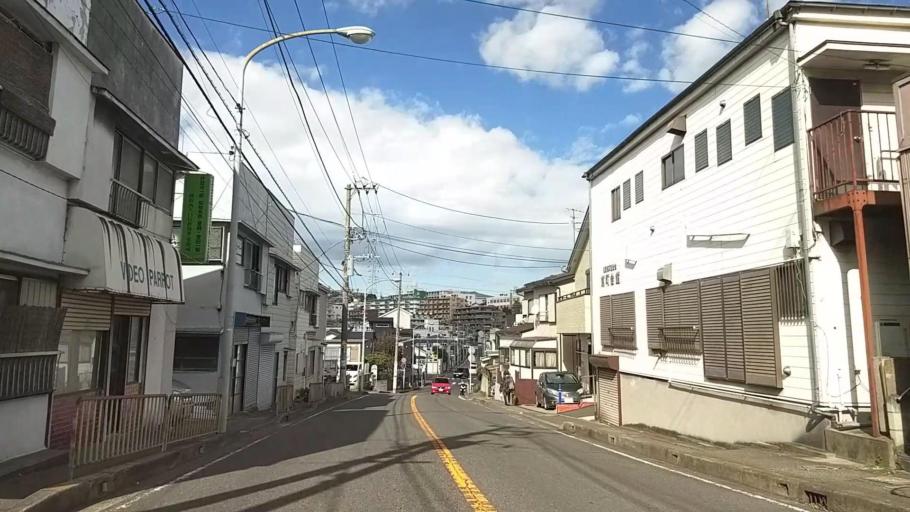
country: JP
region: Kanagawa
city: Yokohama
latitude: 35.4873
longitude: 139.6397
